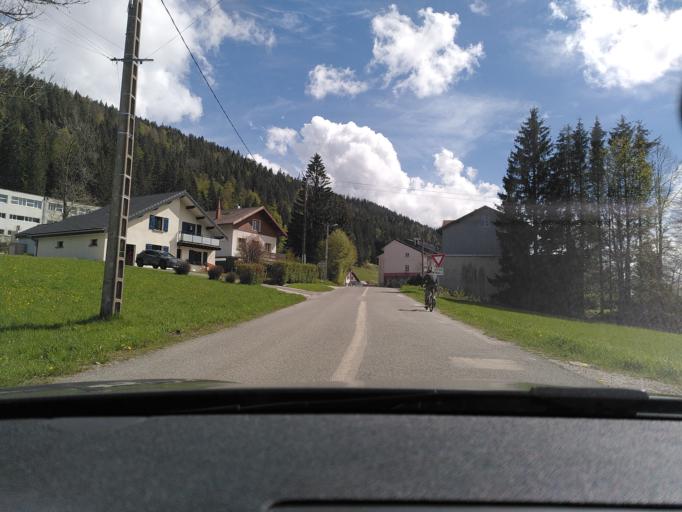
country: FR
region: Franche-Comte
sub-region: Departement du Jura
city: Les Rousses
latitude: 46.5339
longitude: 6.1381
